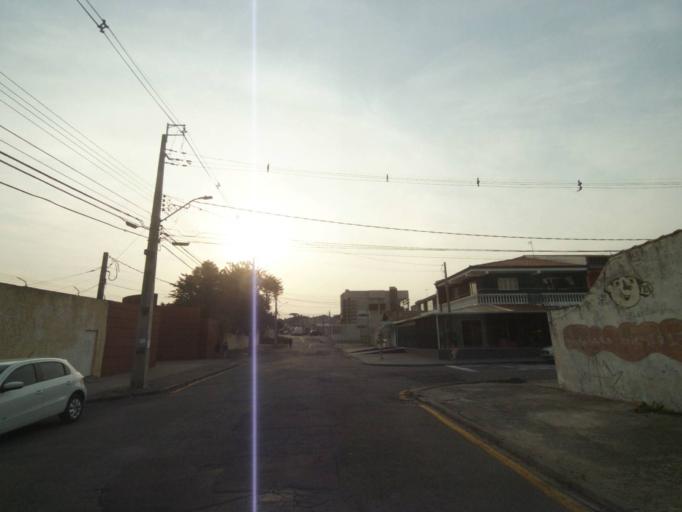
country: BR
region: Parana
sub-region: Pinhais
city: Pinhais
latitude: -25.4851
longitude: -49.2035
